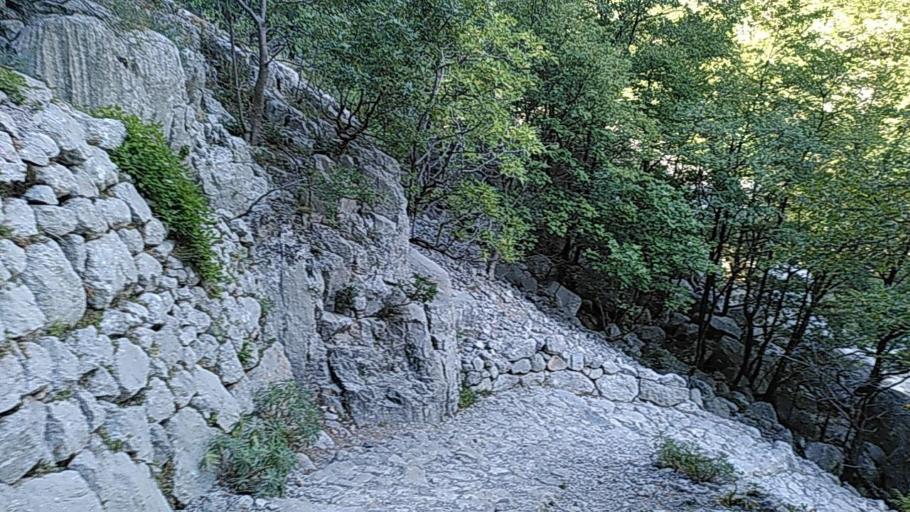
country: HR
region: Zadarska
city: Starigrad
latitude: 44.3081
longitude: 15.4768
